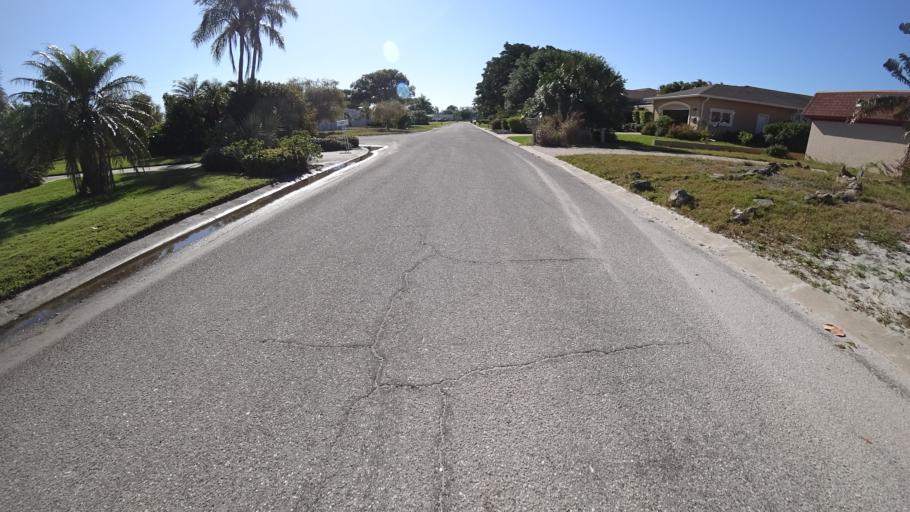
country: US
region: Florida
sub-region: Manatee County
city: Bayshore Gardens
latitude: 27.4216
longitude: -82.5930
